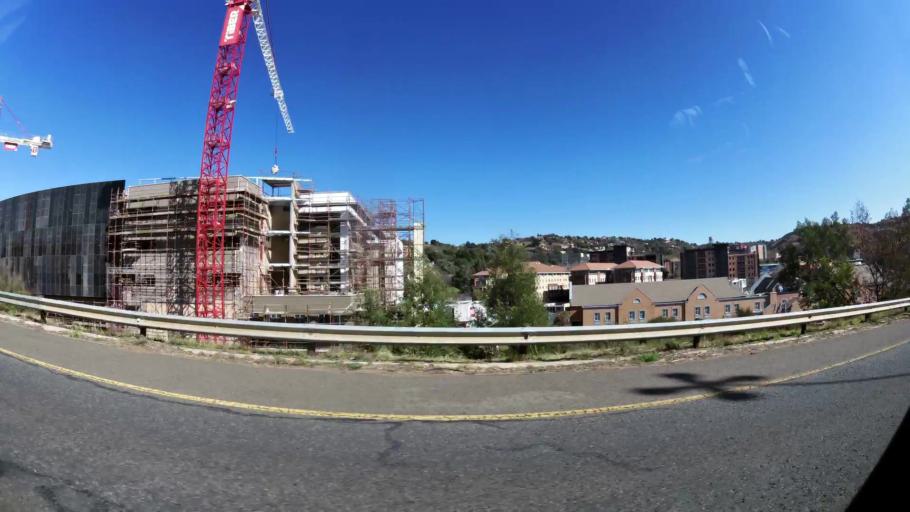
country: ZA
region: Gauteng
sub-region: City of Johannesburg Metropolitan Municipality
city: Roodepoort
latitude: -26.1528
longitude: 27.9253
